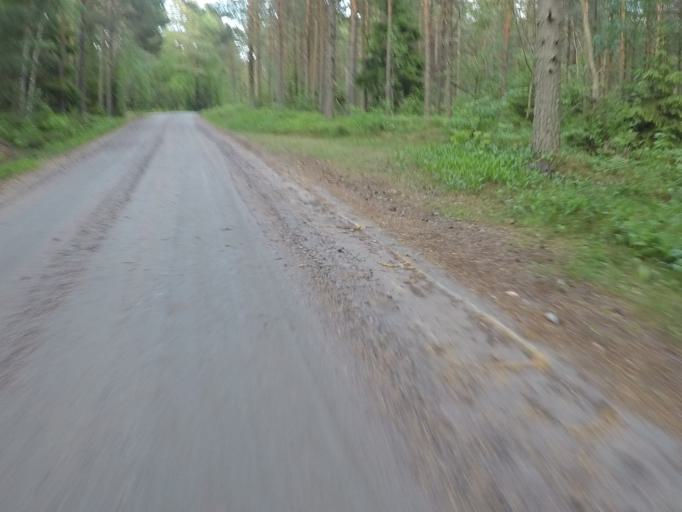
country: SE
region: Soedermanland
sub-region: Eskilstuna Kommun
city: Hallbybrunn
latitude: 59.3938
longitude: 16.3994
